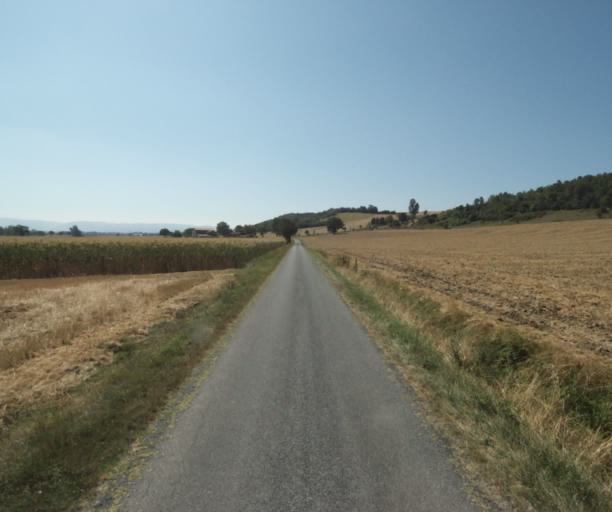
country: FR
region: Midi-Pyrenees
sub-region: Departement du Tarn
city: Puylaurens
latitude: 43.5232
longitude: 1.9420
